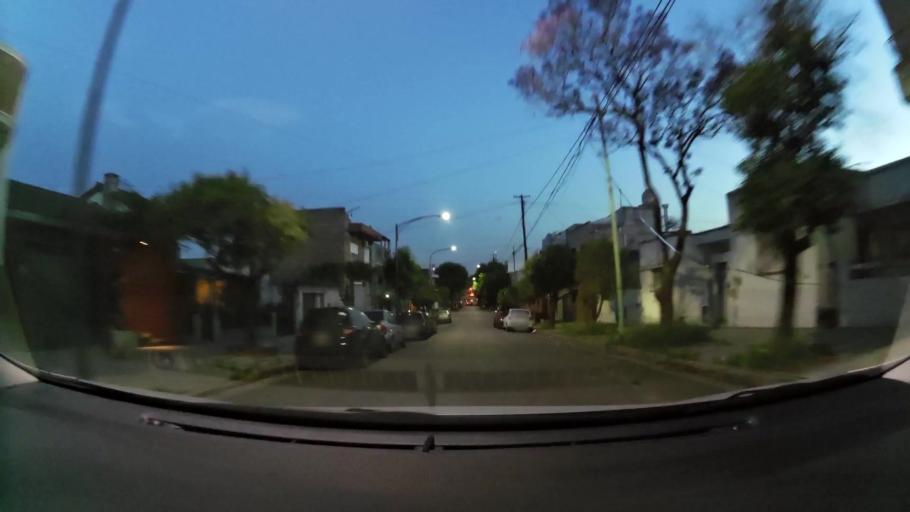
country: AR
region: Buenos Aires F.D.
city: Villa Lugano
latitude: -34.6859
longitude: -58.4809
